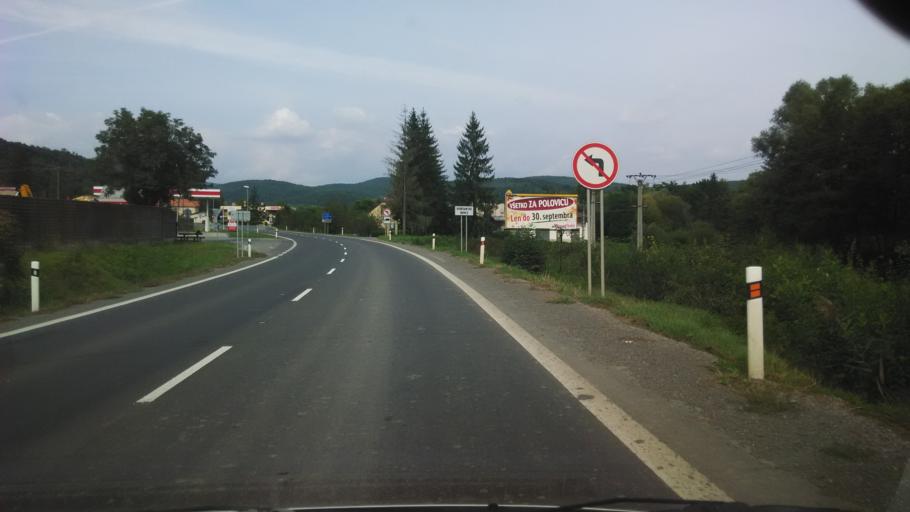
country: SK
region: Banskobystricky
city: Krupina
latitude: 48.2814
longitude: 18.9888
